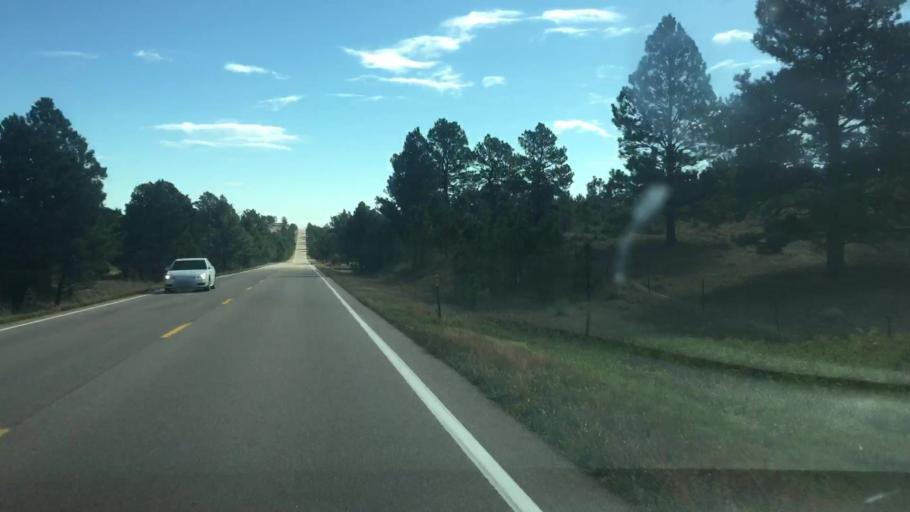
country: US
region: Colorado
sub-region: Elbert County
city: Kiowa
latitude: 39.2736
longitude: -104.2004
